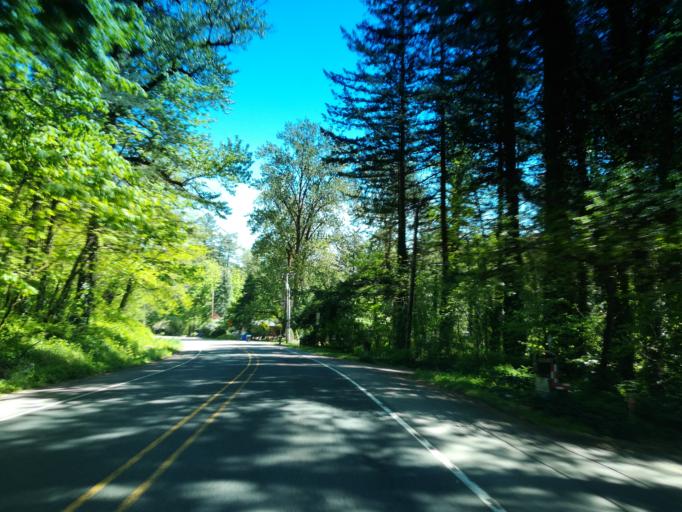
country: US
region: Oregon
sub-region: Multnomah County
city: Troutdale
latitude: 45.5127
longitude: -122.3689
